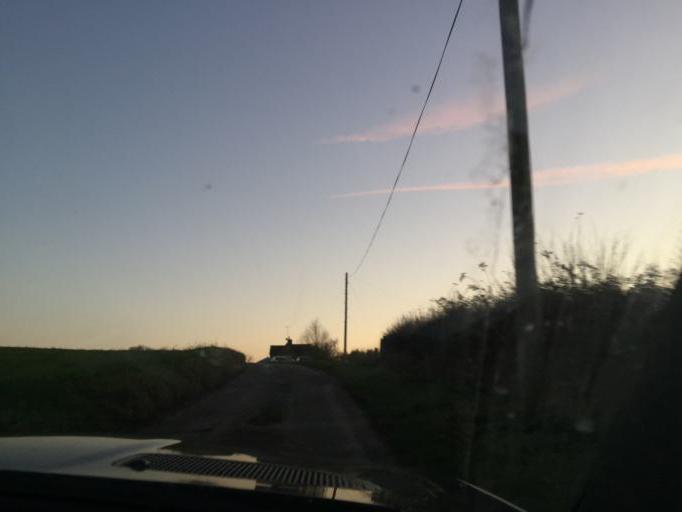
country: GB
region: England
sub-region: Northamptonshire
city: Brackley
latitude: 52.0931
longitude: -1.1123
